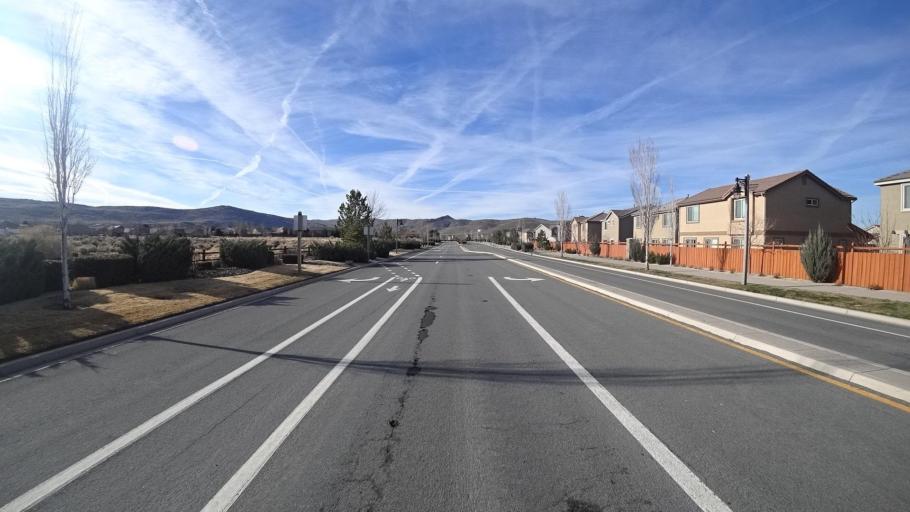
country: US
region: Nevada
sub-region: Washoe County
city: Spanish Springs
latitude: 39.6185
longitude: -119.6702
